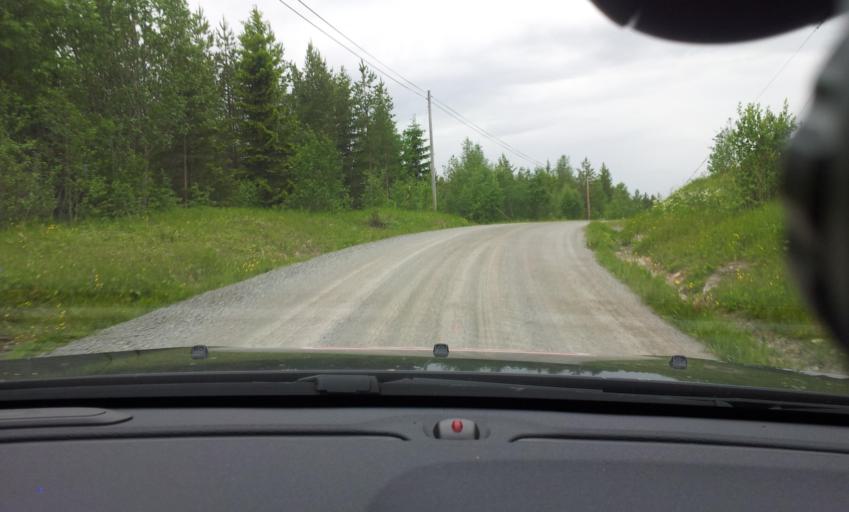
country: SE
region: Jaemtland
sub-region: OEstersunds Kommun
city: Brunflo
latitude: 62.9744
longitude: 14.6679
